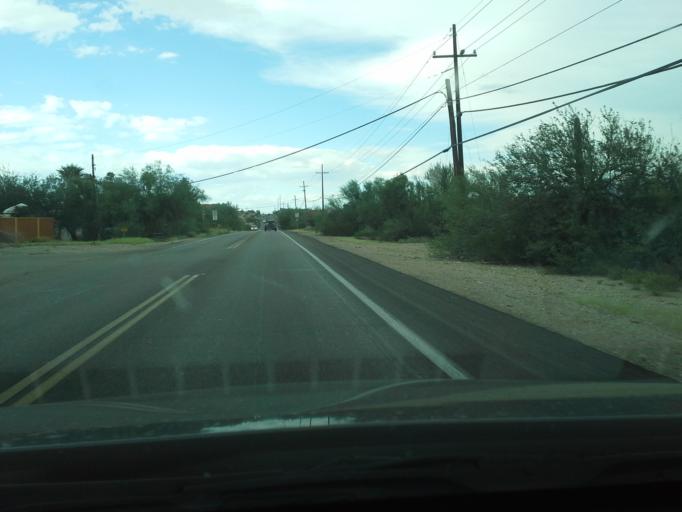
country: US
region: Arizona
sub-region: Pima County
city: South Tucson
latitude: 32.2179
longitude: -111.0203
